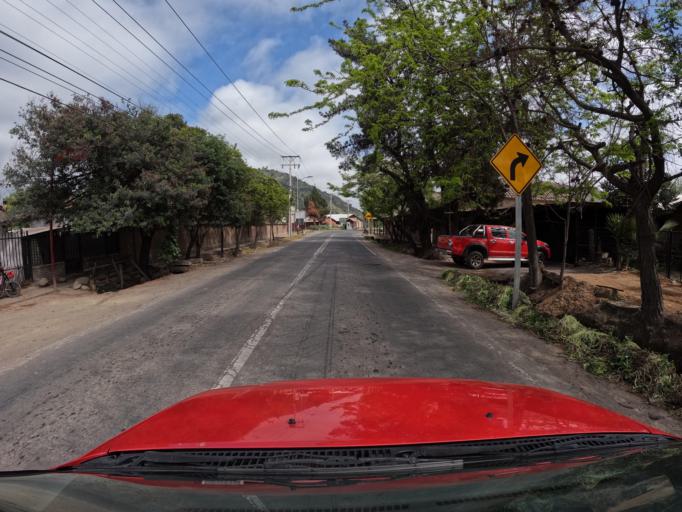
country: CL
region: O'Higgins
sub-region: Provincia de Colchagua
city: Santa Cruz
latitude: -34.7077
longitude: -71.2996
